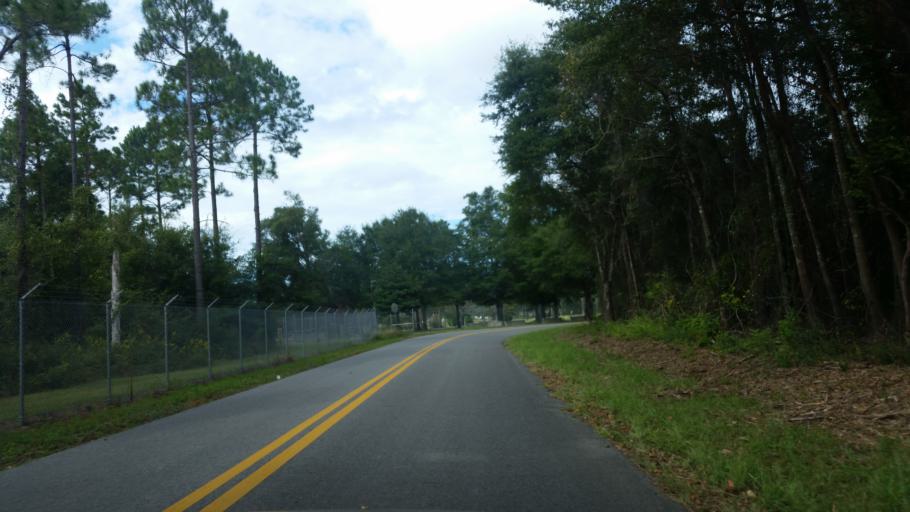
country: US
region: Florida
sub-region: Santa Rosa County
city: Point Baker
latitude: 30.7332
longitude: -87.0130
